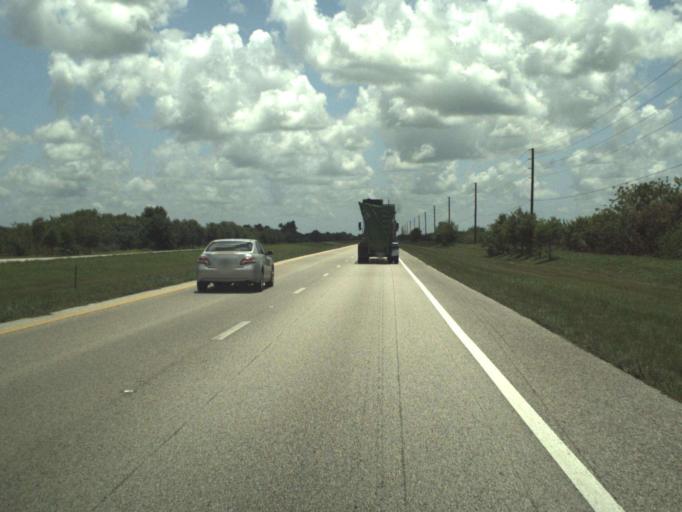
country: US
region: Florida
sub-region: Indian River County
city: Fellsmere
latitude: 27.6417
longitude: -80.7635
